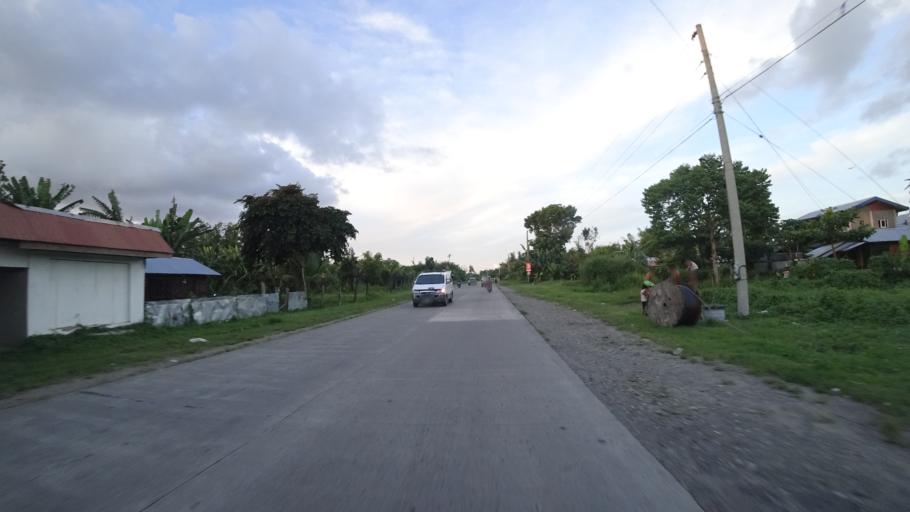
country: PH
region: Eastern Visayas
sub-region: Province of Leyte
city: Palo
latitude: 11.1523
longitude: 124.9995
